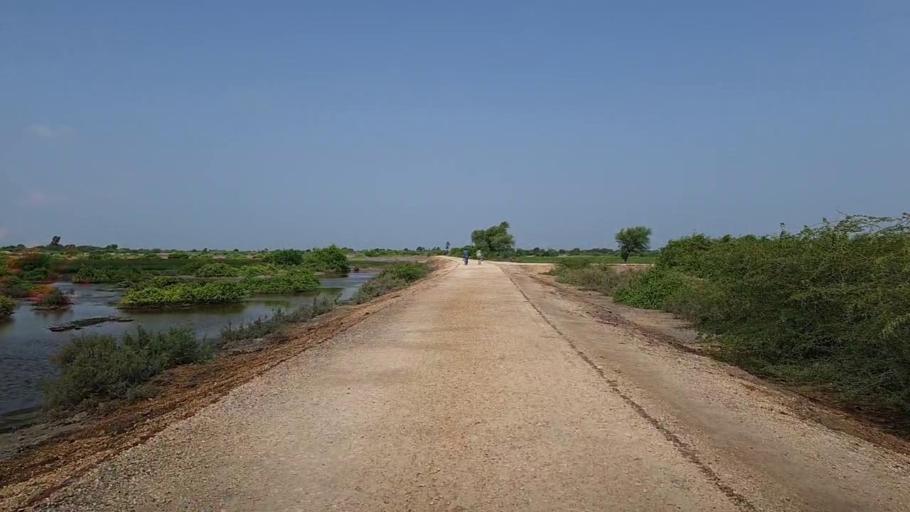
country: PK
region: Sindh
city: Mirpur Batoro
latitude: 24.6491
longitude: 68.4262
